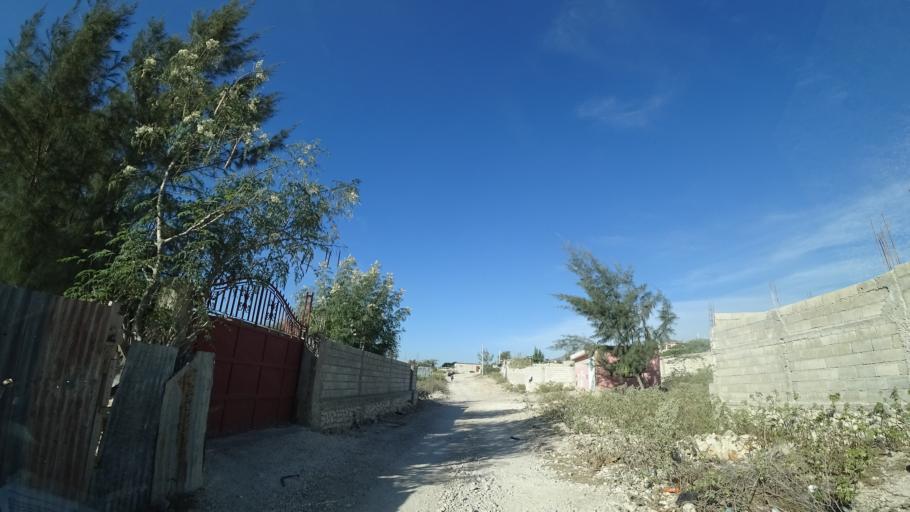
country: HT
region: Ouest
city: Croix des Bouquets
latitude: 18.6697
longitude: -72.2324
